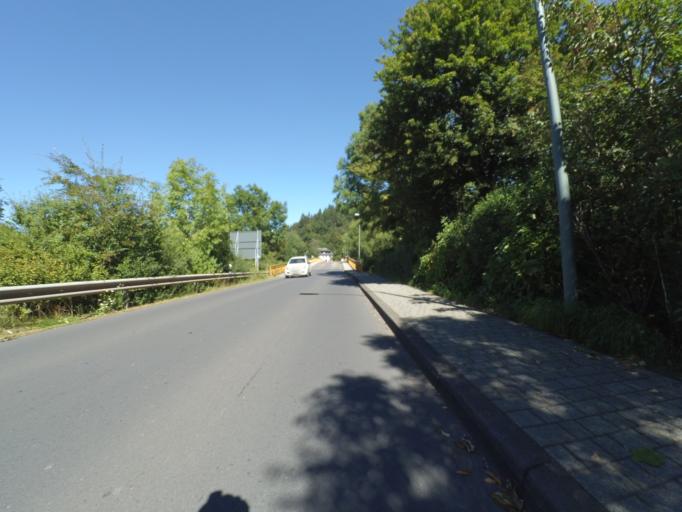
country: DE
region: Rheinland-Pfalz
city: Junkerath
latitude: 50.3478
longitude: 6.5720
